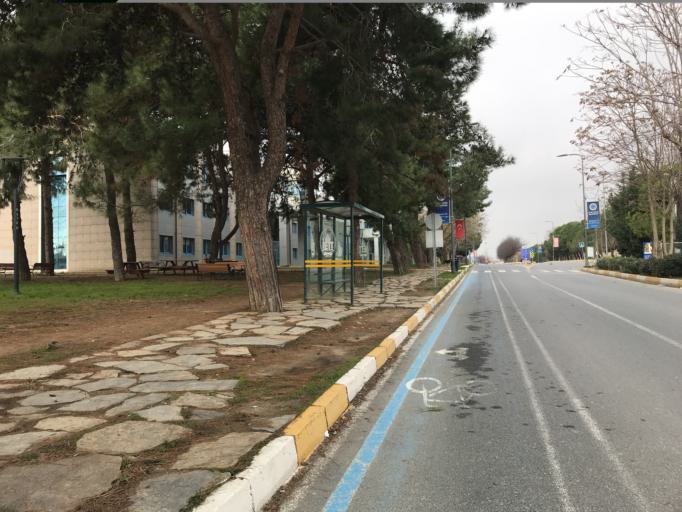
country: TR
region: Istanbul
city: merter keresteciler
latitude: 41.0233
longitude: 28.8896
